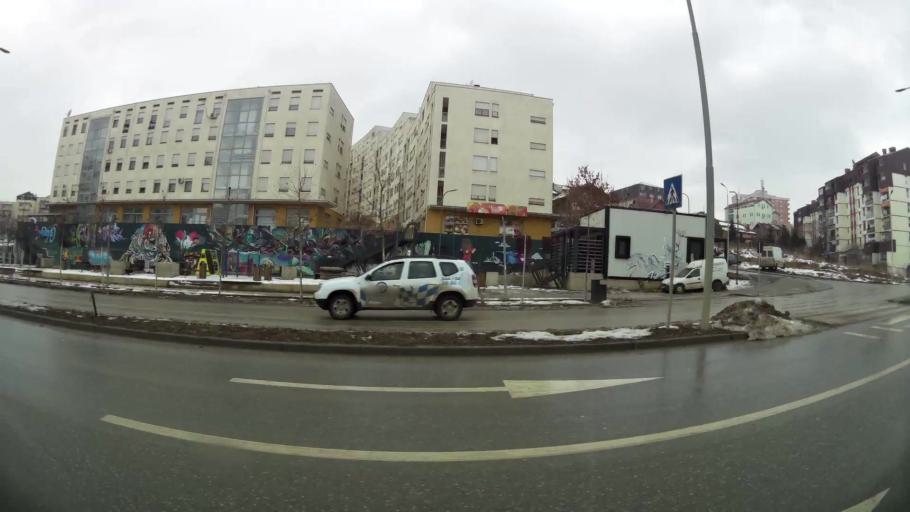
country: XK
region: Pristina
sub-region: Komuna e Prishtines
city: Pristina
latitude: 42.6551
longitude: 21.1781
